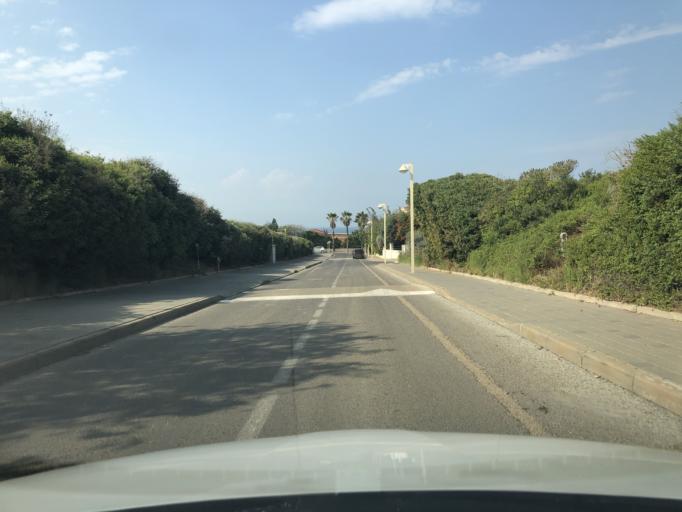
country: IL
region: Tel Aviv
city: Kefar Shemaryahu
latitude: 32.2148
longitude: 34.8173
